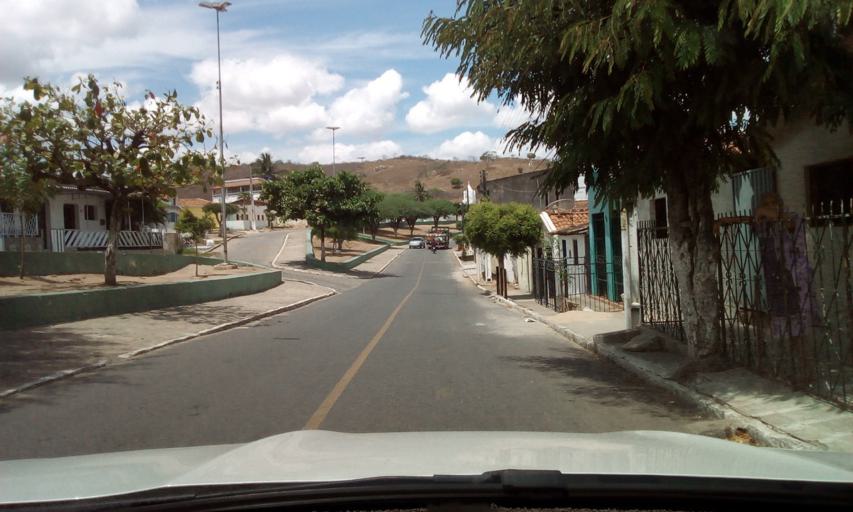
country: BR
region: Paraiba
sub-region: Gurinhem
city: Gurinhem
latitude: -7.1237
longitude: -35.4259
